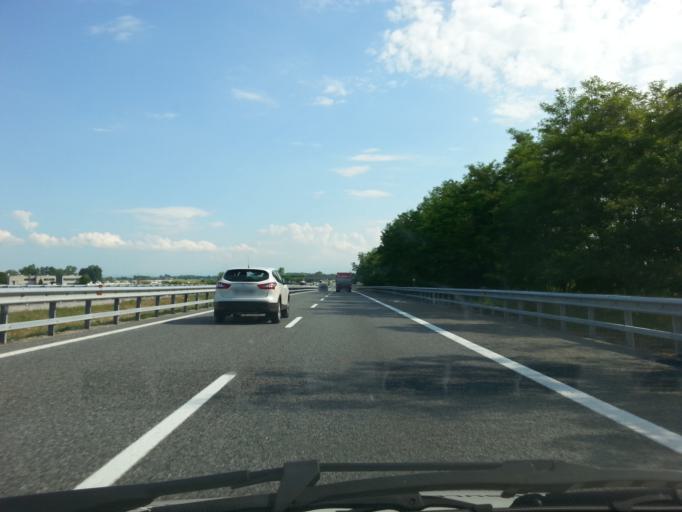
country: IT
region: Piedmont
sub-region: Provincia di Cuneo
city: Caramagna Piemonte
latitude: 44.7974
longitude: 7.7525
